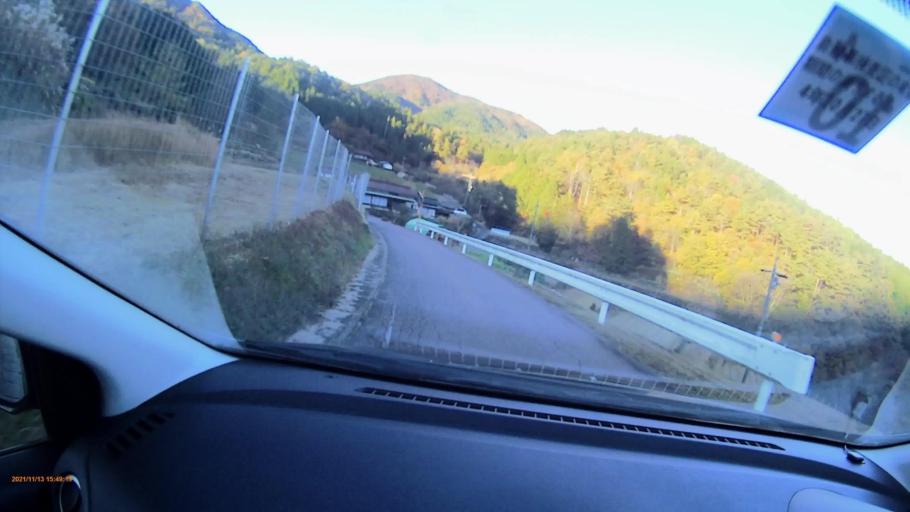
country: JP
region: Gifu
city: Nakatsugawa
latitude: 35.5977
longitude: 137.4080
